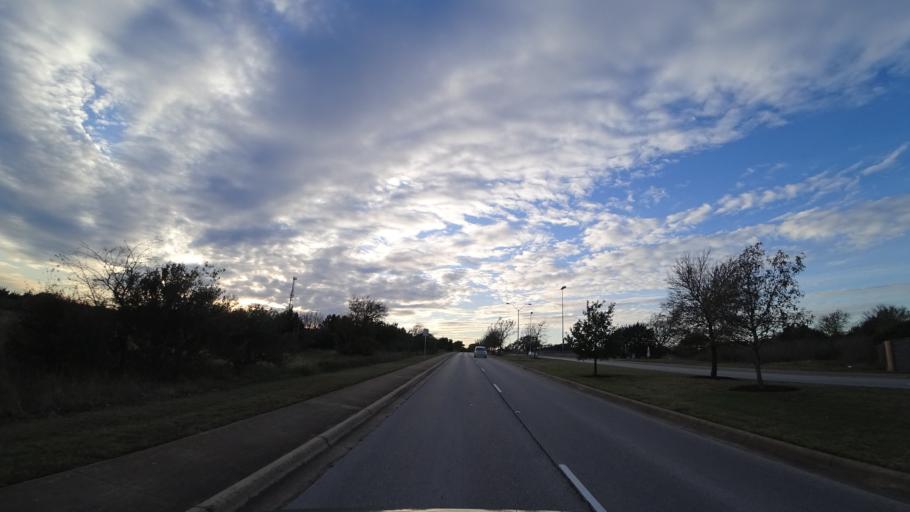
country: US
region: Texas
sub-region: Williamson County
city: Brushy Creek
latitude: 30.4951
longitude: -97.7308
